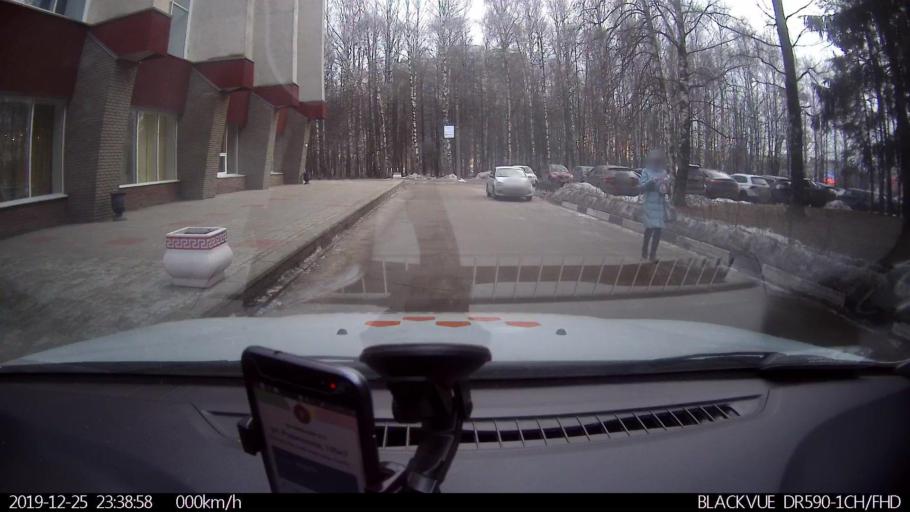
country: RU
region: Nizjnij Novgorod
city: Bor
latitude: 56.3113
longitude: 44.0770
